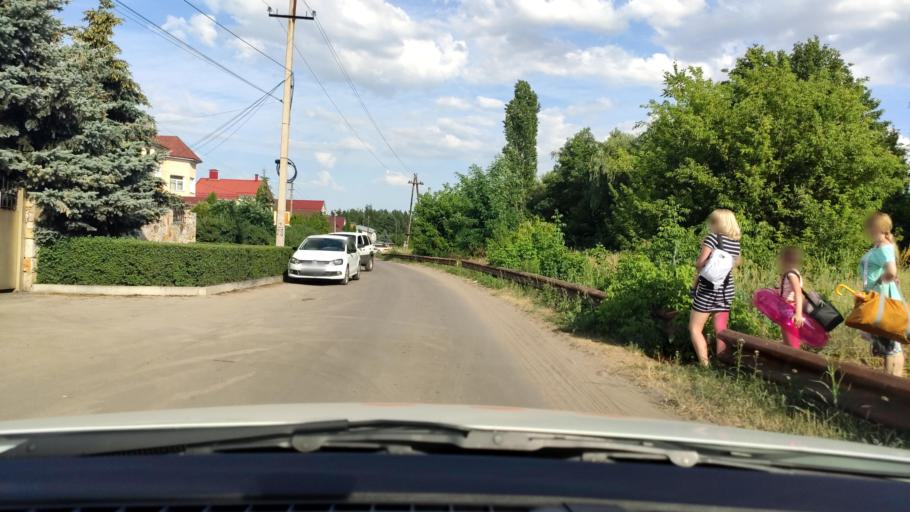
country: RU
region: Voronezj
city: Novaya Usman'
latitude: 51.6293
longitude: 39.4185
